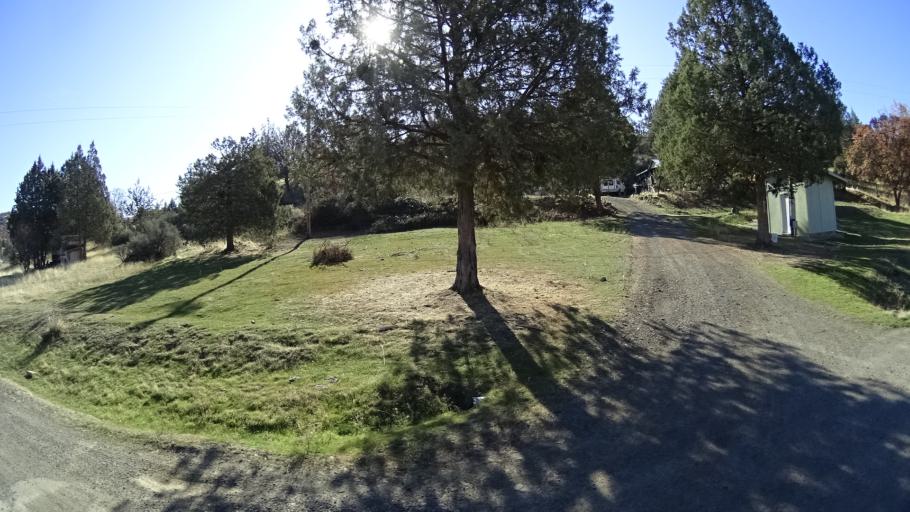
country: US
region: California
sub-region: Siskiyou County
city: Montague
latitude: 41.8945
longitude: -122.5232
